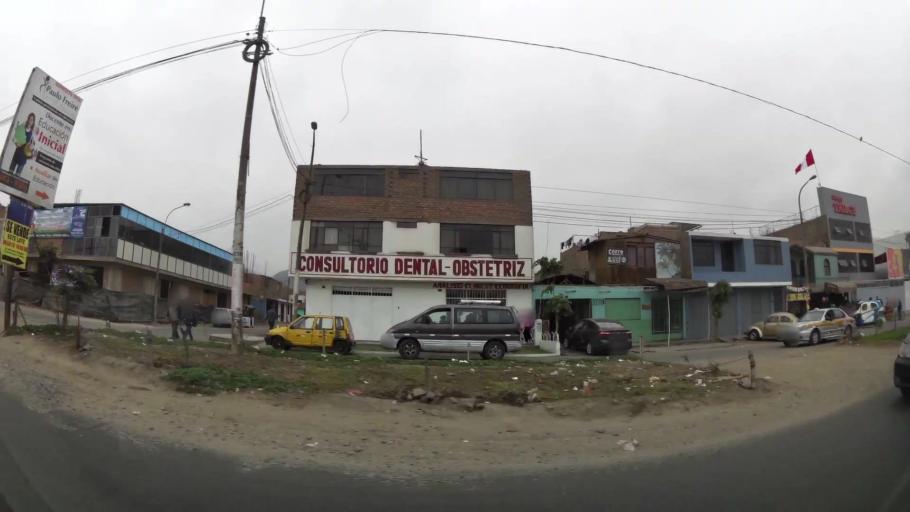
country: PE
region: Lima
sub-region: Lima
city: Independencia
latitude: -11.9531
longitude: -77.0598
